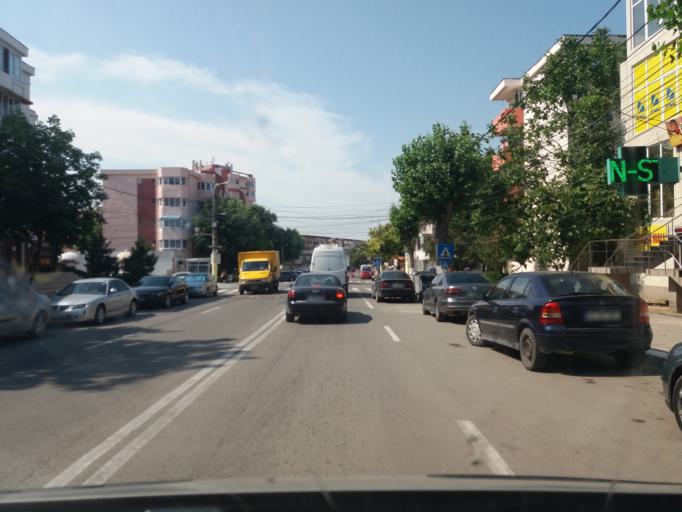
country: RO
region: Constanta
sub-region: Comuna Navodari
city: Navodari
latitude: 44.3193
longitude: 28.6093
